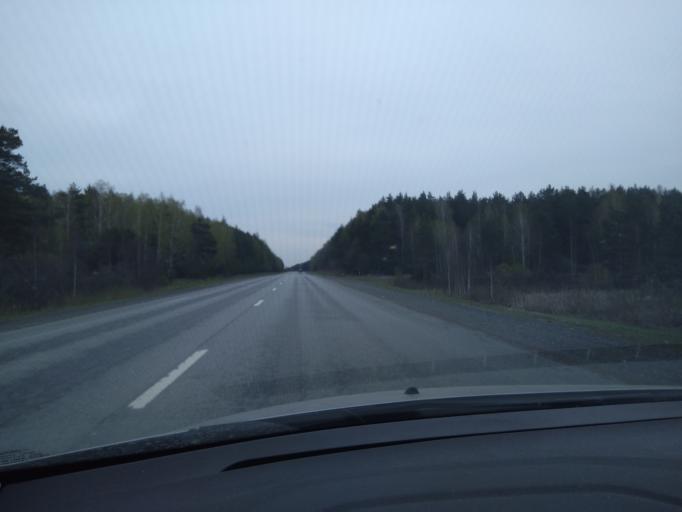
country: RU
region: Sverdlovsk
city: Baraba
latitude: 56.7830
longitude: 61.7701
